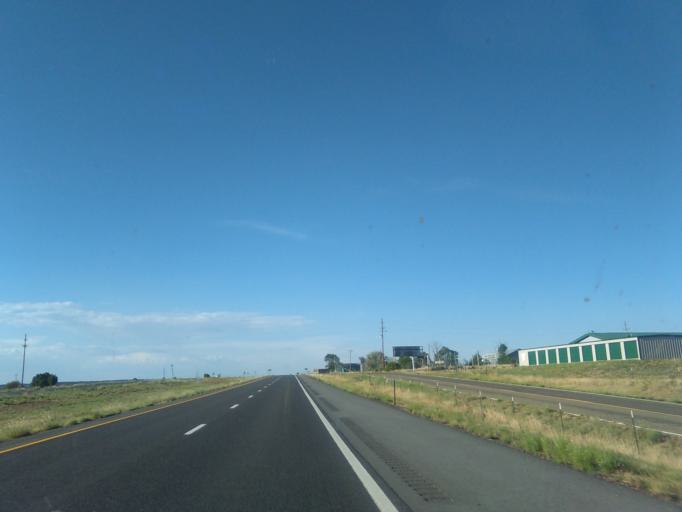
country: US
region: New Mexico
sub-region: San Miguel County
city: Las Vegas
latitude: 35.6546
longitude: -105.1899
